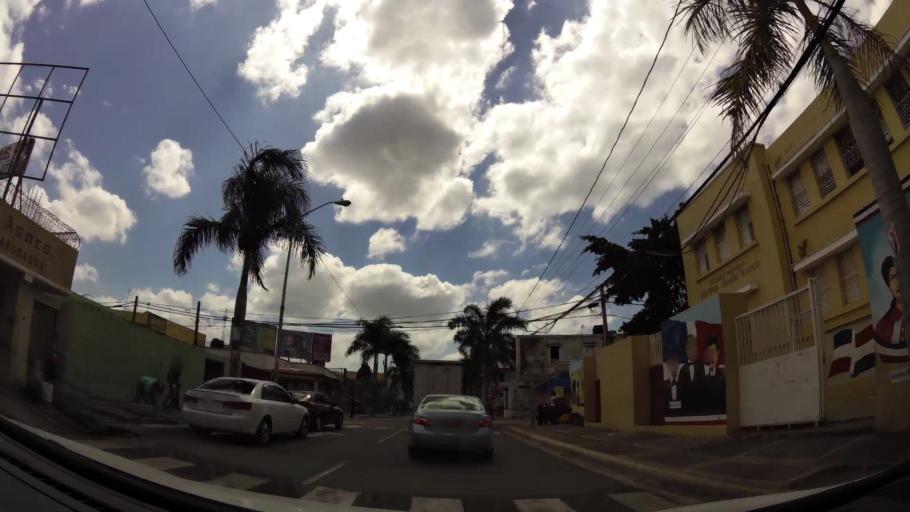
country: DO
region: San Cristobal
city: San Cristobal
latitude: 18.4198
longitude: -70.1135
